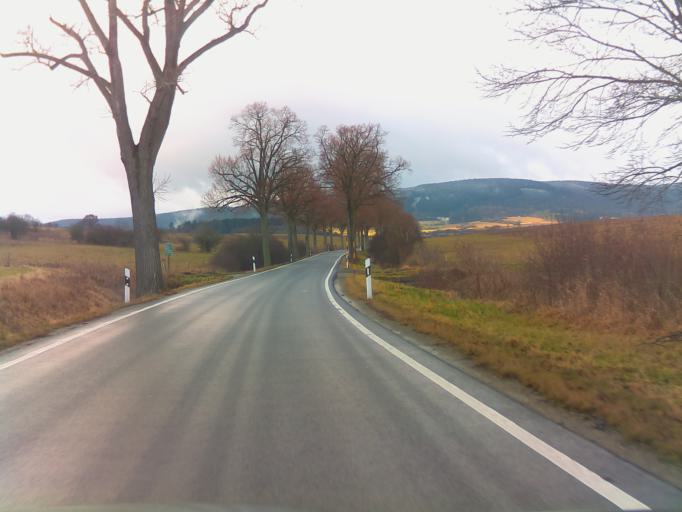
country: DE
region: Thuringia
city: Gossel
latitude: 50.7905
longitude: 10.8207
